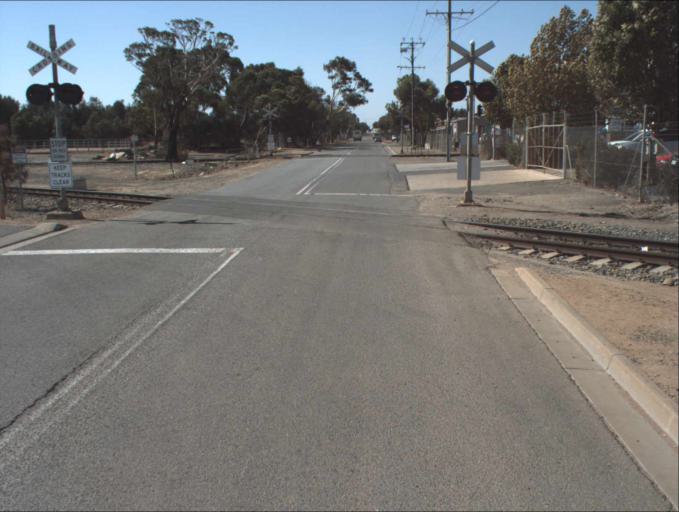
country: AU
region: South Australia
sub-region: Port Adelaide Enfield
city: Blair Athol
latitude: -34.8389
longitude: 138.5817
